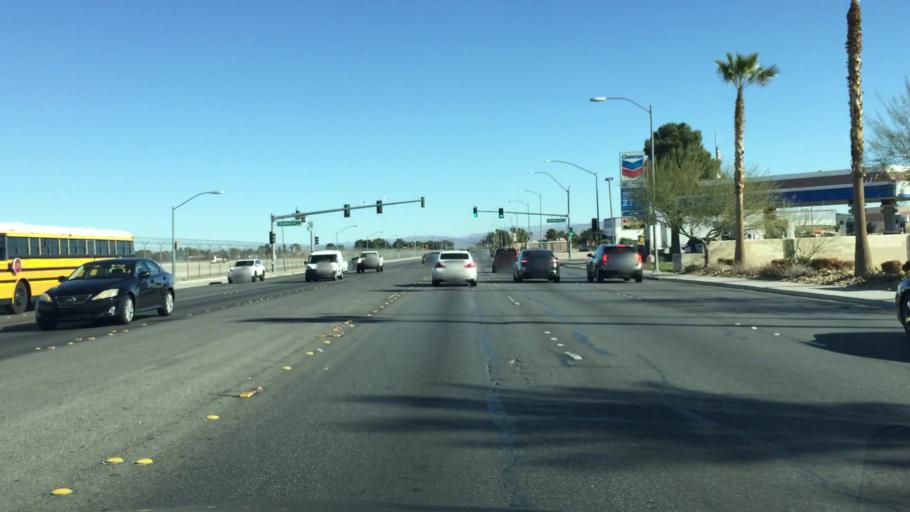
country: US
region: Nevada
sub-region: Clark County
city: Paradise
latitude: 36.0717
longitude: -115.1288
